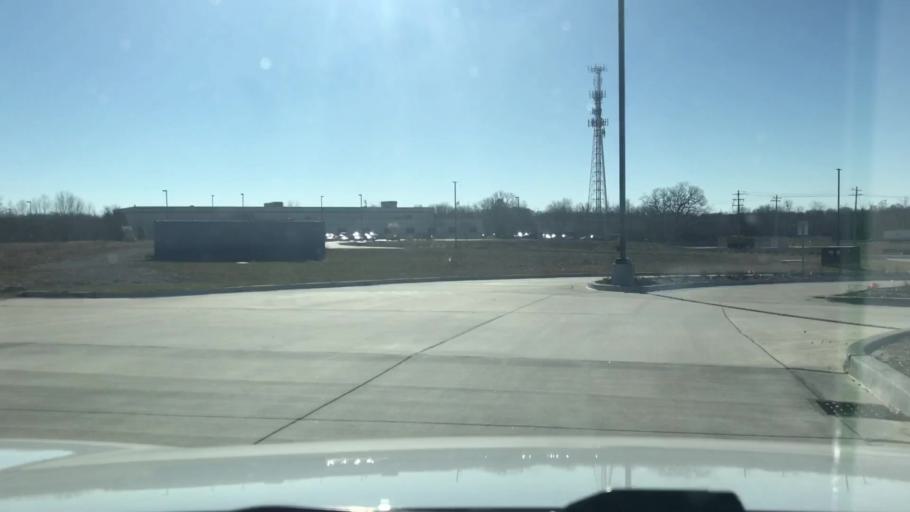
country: US
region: Illinois
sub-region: Saint Clair County
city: Alorton
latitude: 38.5633
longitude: -90.0824
